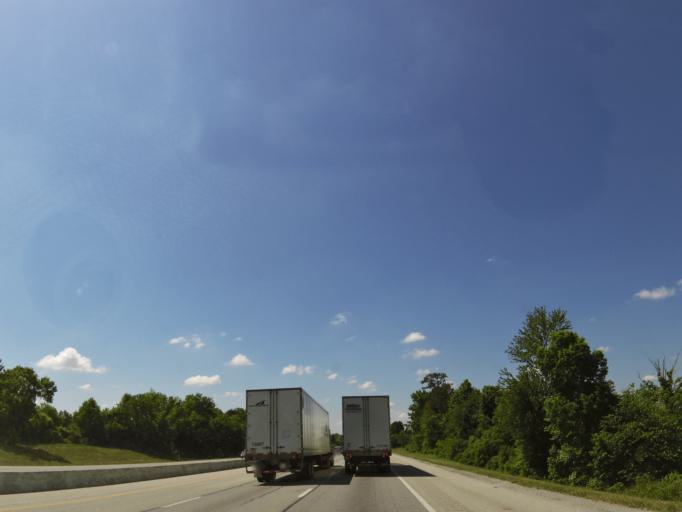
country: US
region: Kentucky
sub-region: Laurel County
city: London
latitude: 37.0826
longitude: -84.0997
